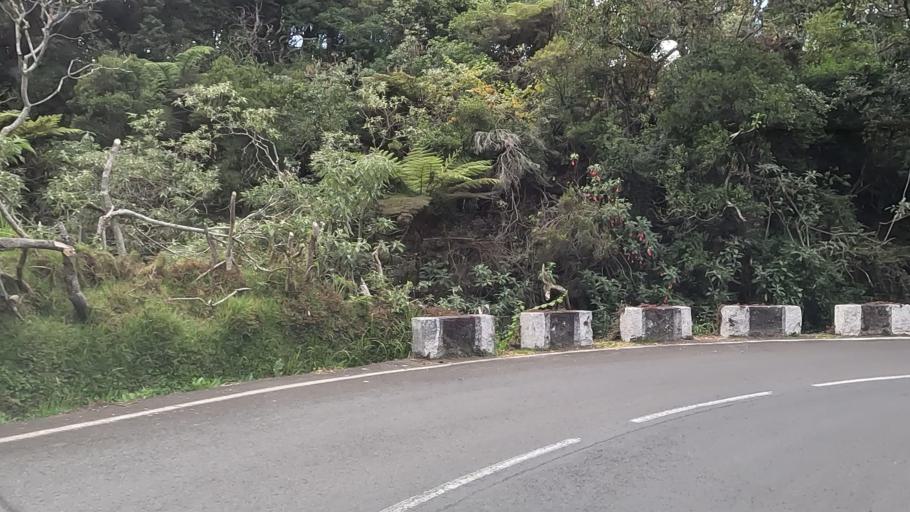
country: RE
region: Reunion
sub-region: Reunion
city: Le Tampon
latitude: -21.2432
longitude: 55.5883
